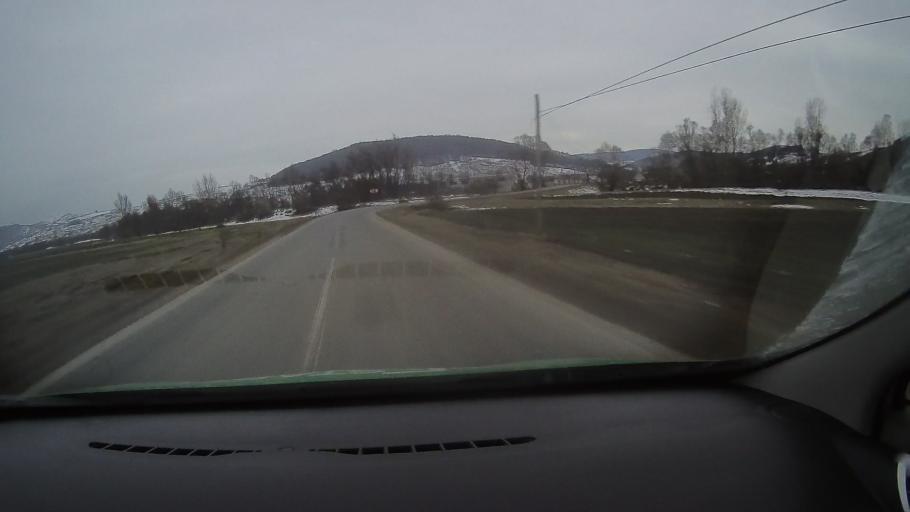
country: RO
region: Harghita
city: Taureni
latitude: 46.2636
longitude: 25.2515
